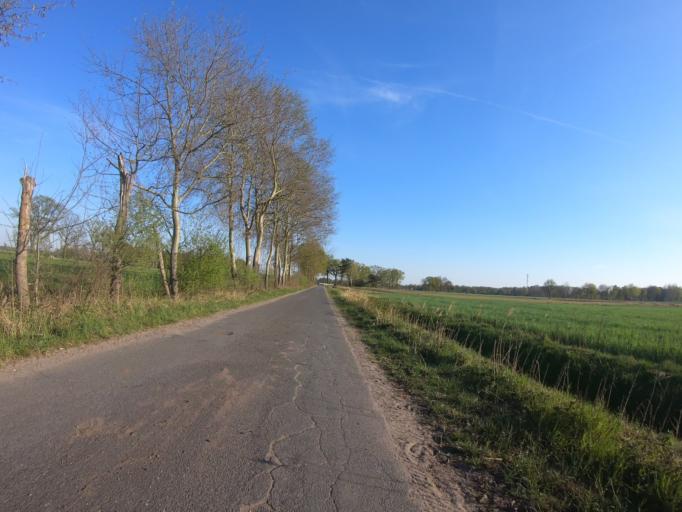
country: DE
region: Lower Saxony
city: Wagenhoff
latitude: 52.5339
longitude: 10.5377
